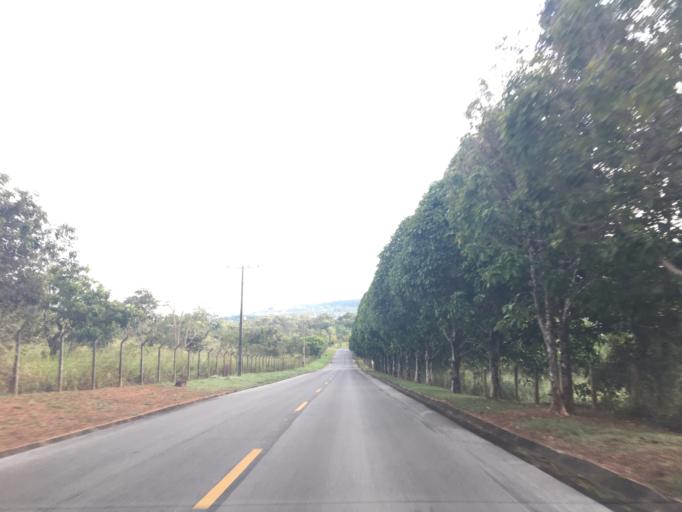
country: BR
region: Federal District
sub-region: Brasilia
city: Brasilia
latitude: -15.8001
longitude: -47.7998
